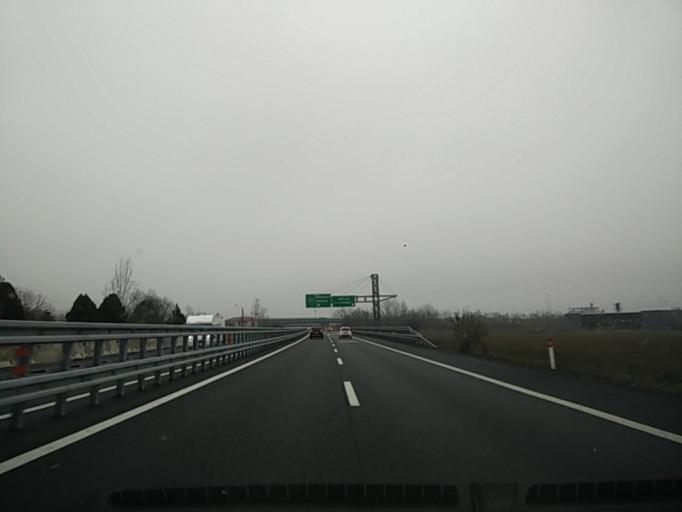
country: IT
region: Piedmont
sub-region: Provincia di Asti
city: Asti
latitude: 44.9113
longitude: 8.2384
